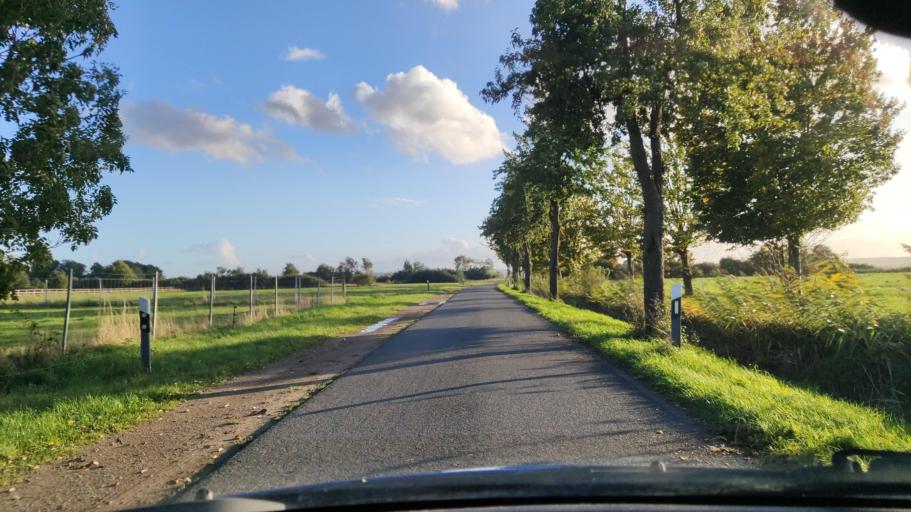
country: DE
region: Lower Saxony
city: Neu Darchau
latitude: 53.2862
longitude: 10.8758
